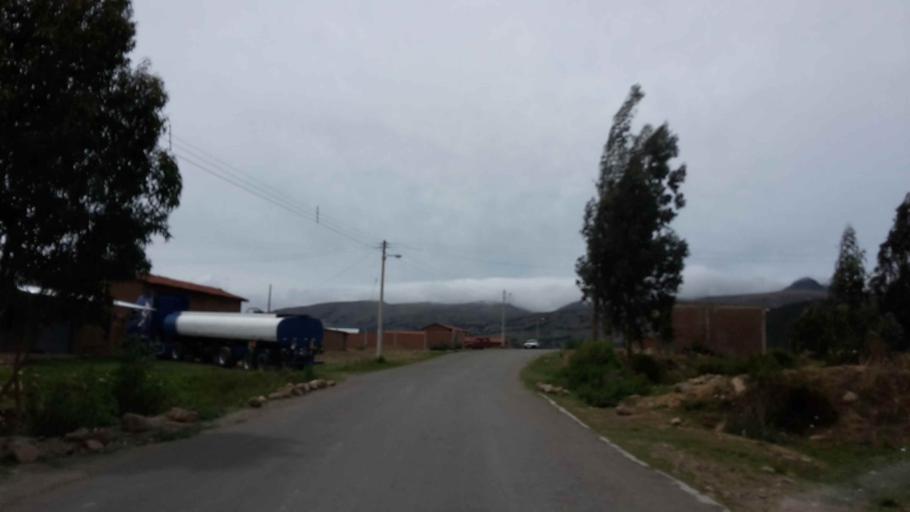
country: BO
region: Cochabamba
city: Arani
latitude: -17.4553
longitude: -65.7187
